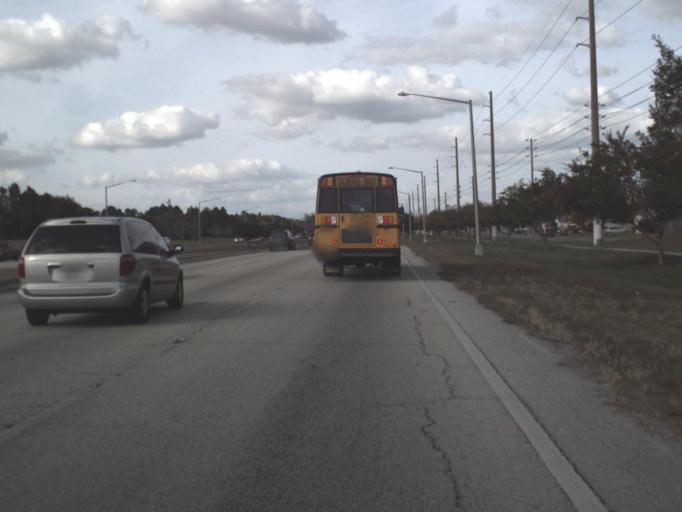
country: US
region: Florida
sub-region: Orange County
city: Williamsburg
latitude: 28.3985
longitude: -81.4249
